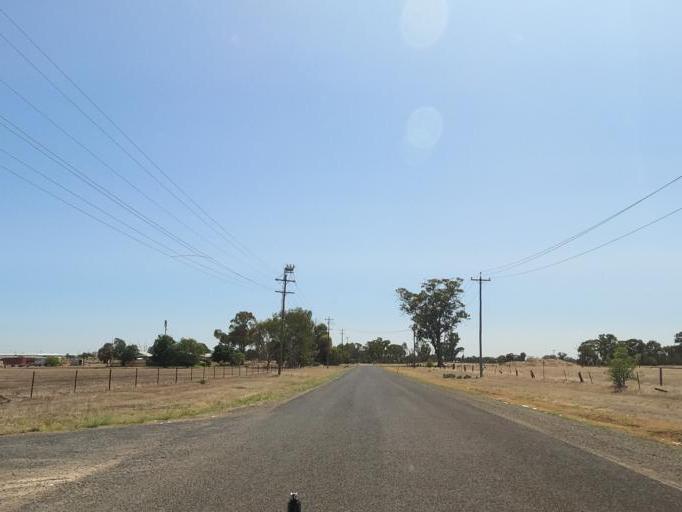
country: AU
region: New South Wales
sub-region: Corowa Shire
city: Mulwala
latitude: -35.9805
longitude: 146.0036
